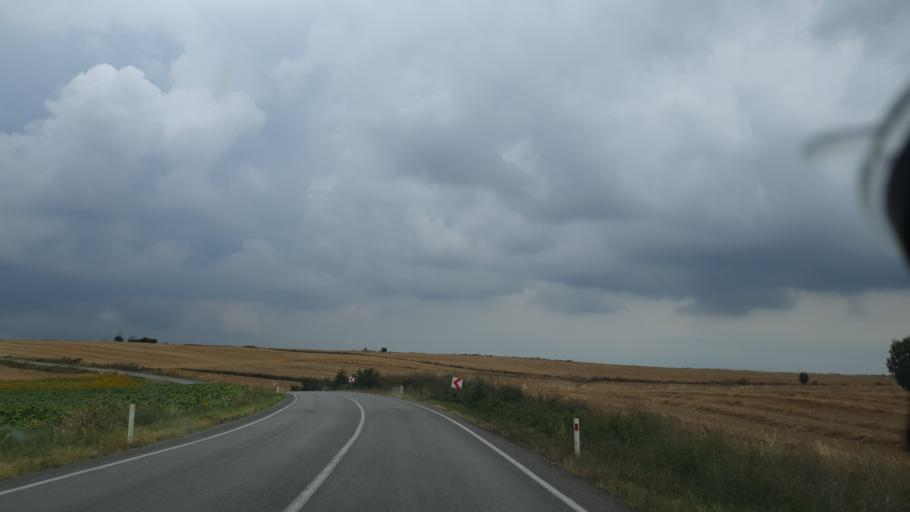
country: TR
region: Tekirdag
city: Hayrabolu
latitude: 41.2281
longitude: 27.0369
